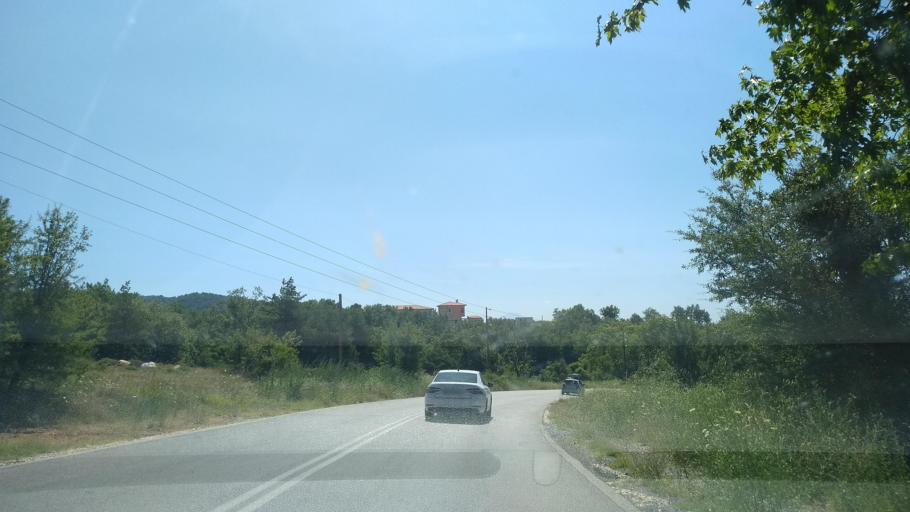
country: GR
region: Central Macedonia
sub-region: Nomos Chalkidikis
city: Megali Panagia
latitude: 40.4549
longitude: 23.6579
